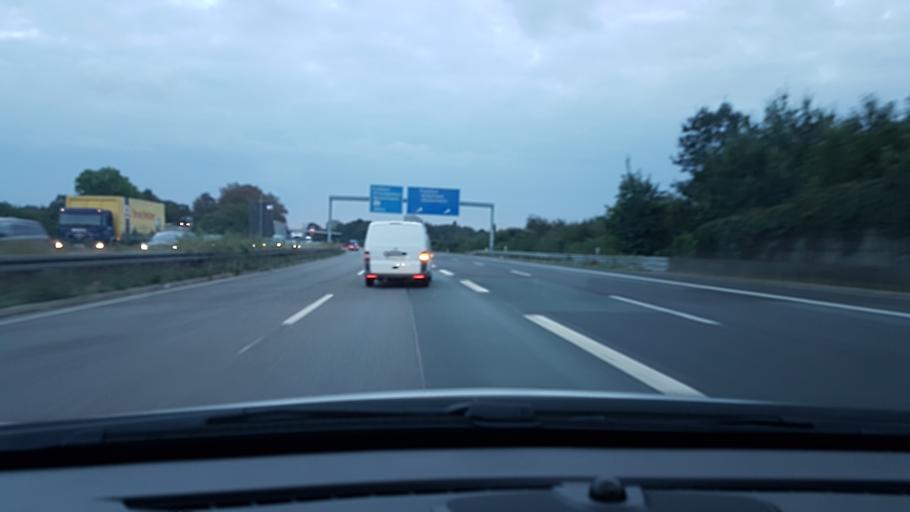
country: DE
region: Hesse
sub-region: Regierungsbezirk Darmstadt
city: Frankfurt am Main
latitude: 50.1614
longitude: 8.6718
